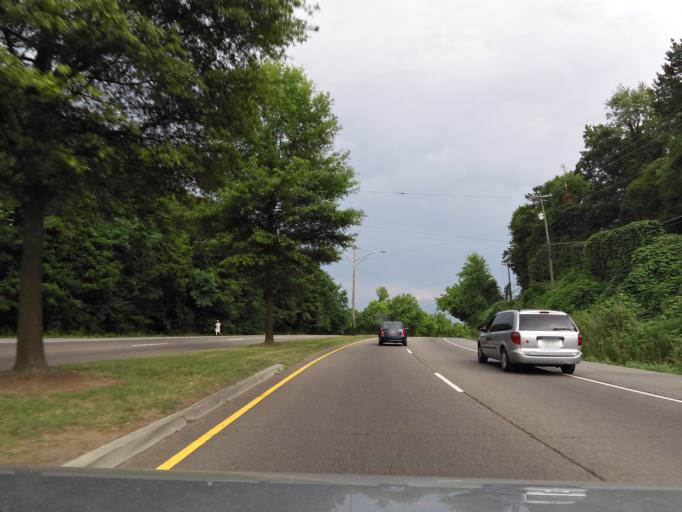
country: US
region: Tennessee
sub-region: Knox County
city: Knoxville
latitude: 36.0539
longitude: -83.9238
